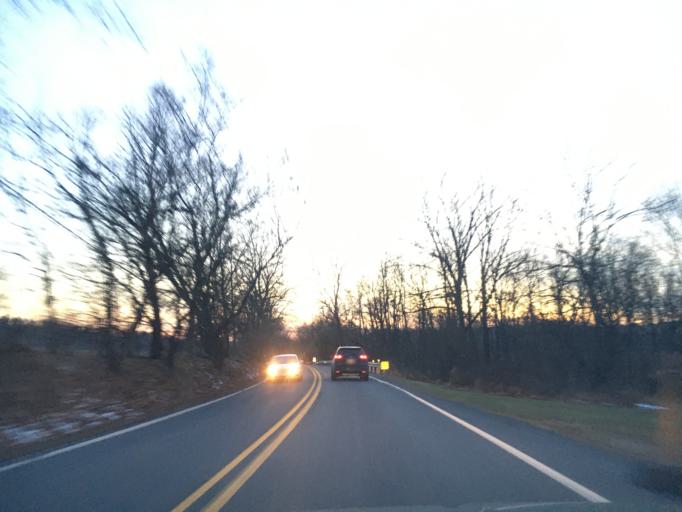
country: US
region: Pennsylvania
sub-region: Northampton County
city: Youngsville
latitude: 40.7523
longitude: -75.4709
